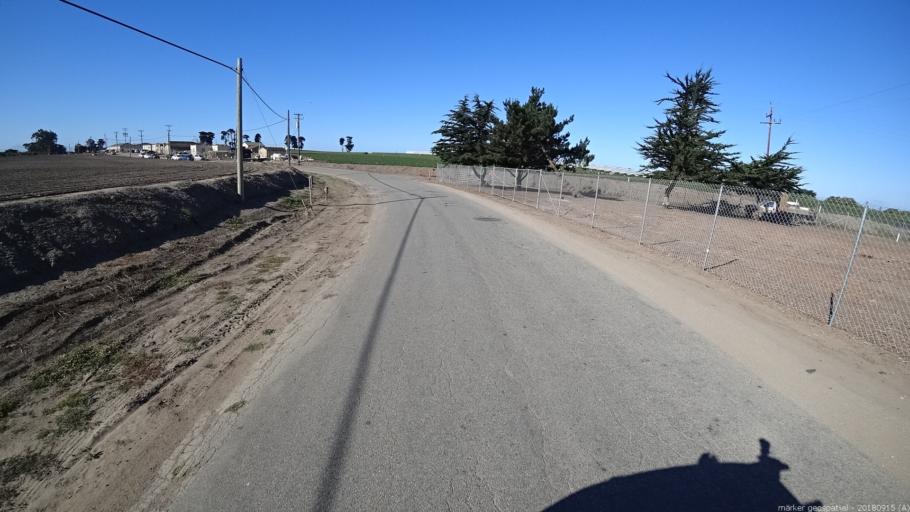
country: US
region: California
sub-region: Monterey County
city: Elkhorn
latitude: 36.8308
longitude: -121.7796
